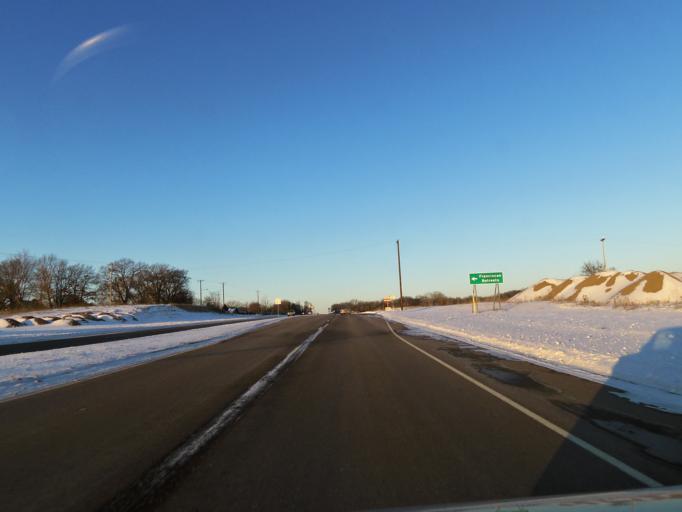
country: US
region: Minnesota
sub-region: Scott County
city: Prior Lake
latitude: 44.7176
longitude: -93.3878
